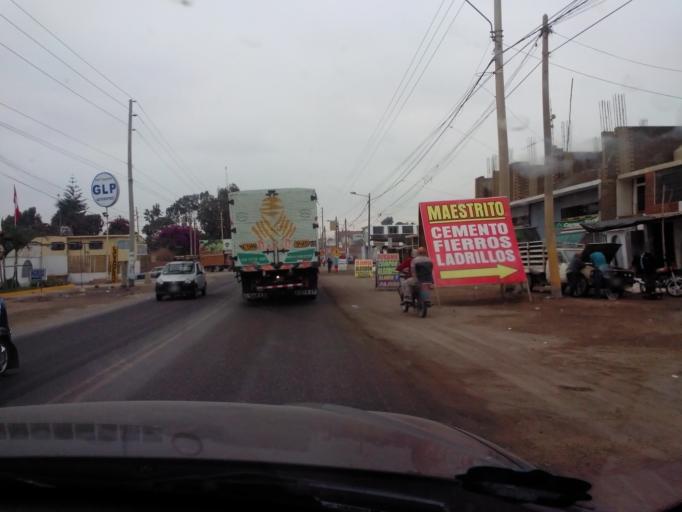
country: PE
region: Ica
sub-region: Provincia de Chincha
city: Chincha Baja
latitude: -13.4444
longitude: -76.1355
